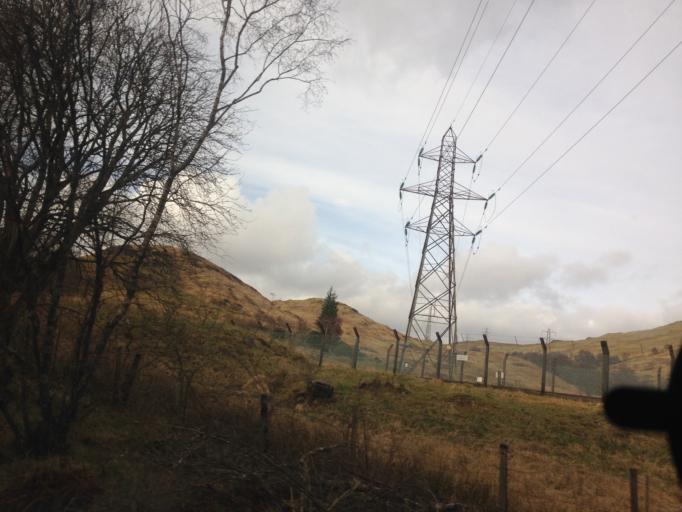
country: GB
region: Scotland
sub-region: Argyll and Bute
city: Garelochhead
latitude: 56.1620
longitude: -4.7795
